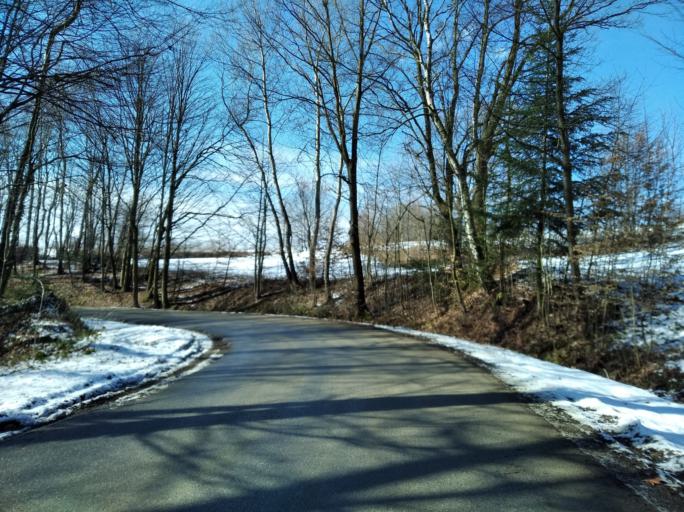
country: PL
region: Subcarpathian Voivodeship
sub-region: Powiat brzozowski
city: Jablonica Polska
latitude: 49.7203
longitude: 21.8835
